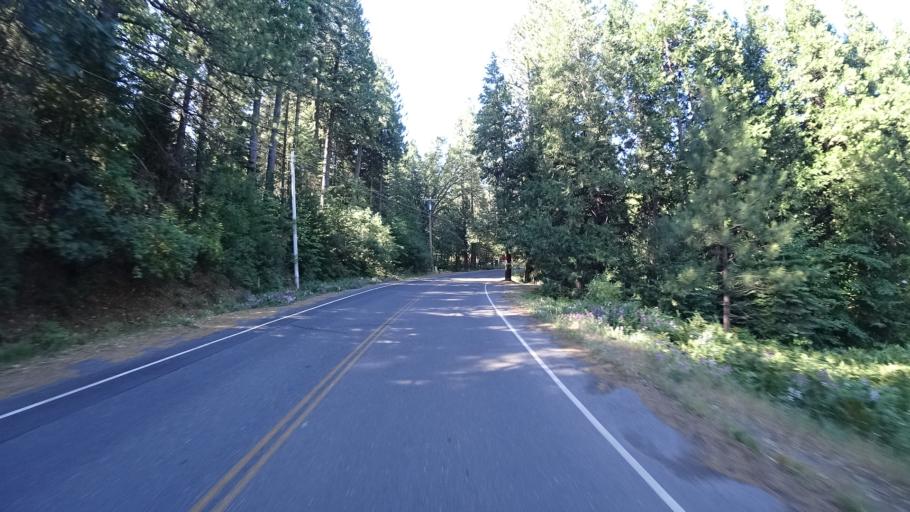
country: US
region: California
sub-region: Calaveras County
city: Arnold
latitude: 38.2595
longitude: -120.3432
